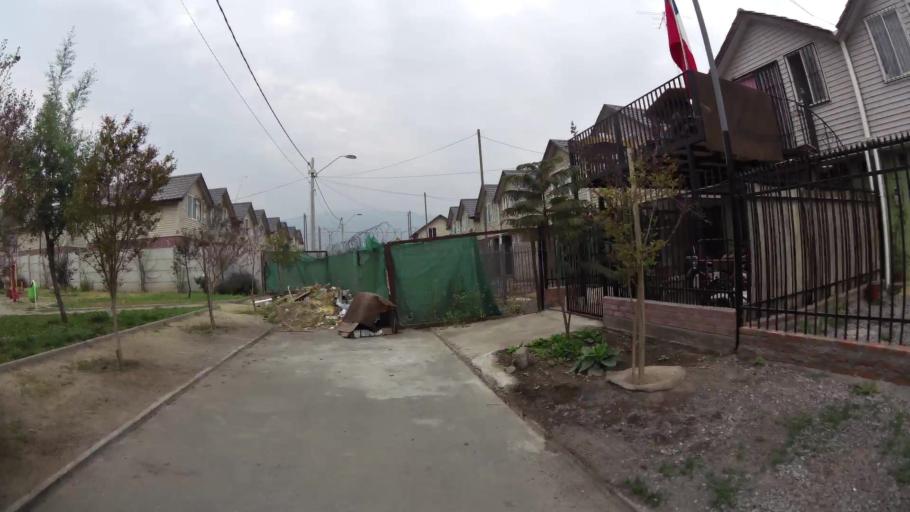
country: CL
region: Santiago Metropolitan
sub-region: Provincia de Chacabuco
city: Chicureo Abajo
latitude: -33.1956
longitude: -70.6656
